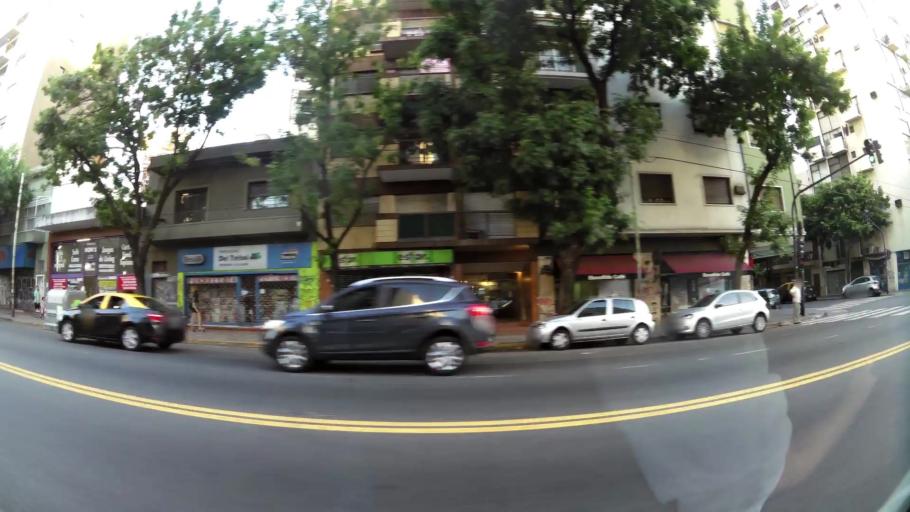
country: AR
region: Buenos Aires F.D.
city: Colegiales
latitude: -34.5896
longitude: -58.4230
